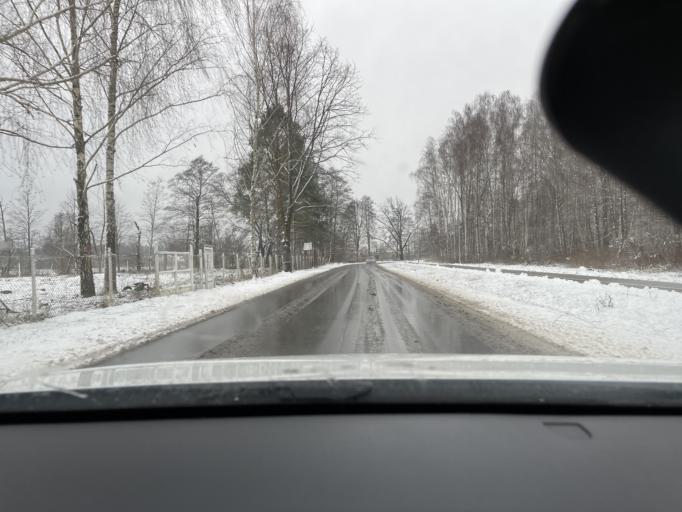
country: PL
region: Masovian Voivodeship
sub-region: Powiat zyrardowski
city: Zyrardow
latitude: 52.0377
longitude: 20.4495
